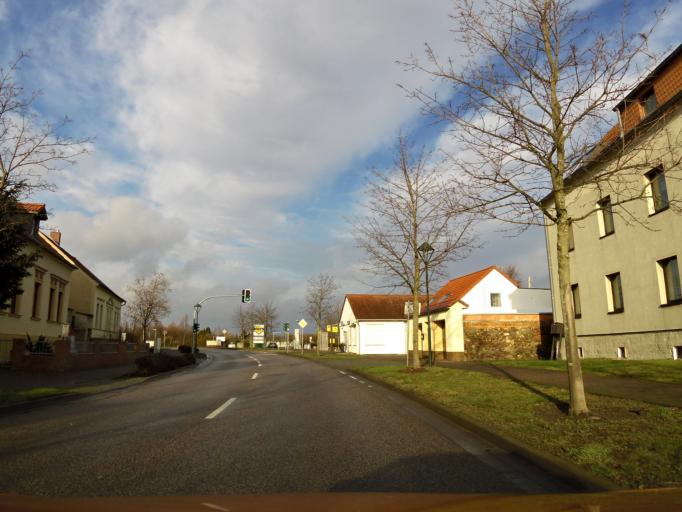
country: DE
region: Saxony-Anhalt
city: Ebendorf
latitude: 52.1846
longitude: 11.5717
